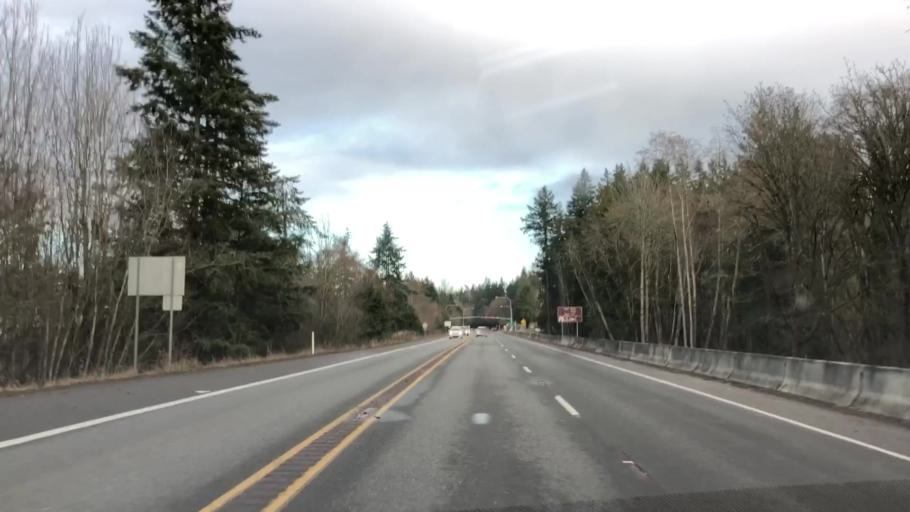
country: US
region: Washington
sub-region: Kitsap County
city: Bainbridge Island
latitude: 47.6323
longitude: -122.5160
